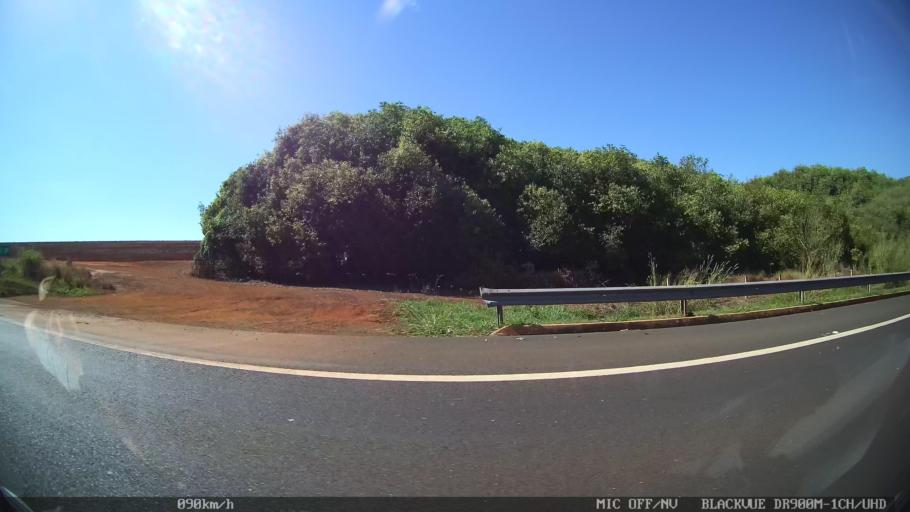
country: BR
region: Sao Paulo
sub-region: Batatais
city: Batatais
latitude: -20.7567
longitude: -47.5315
